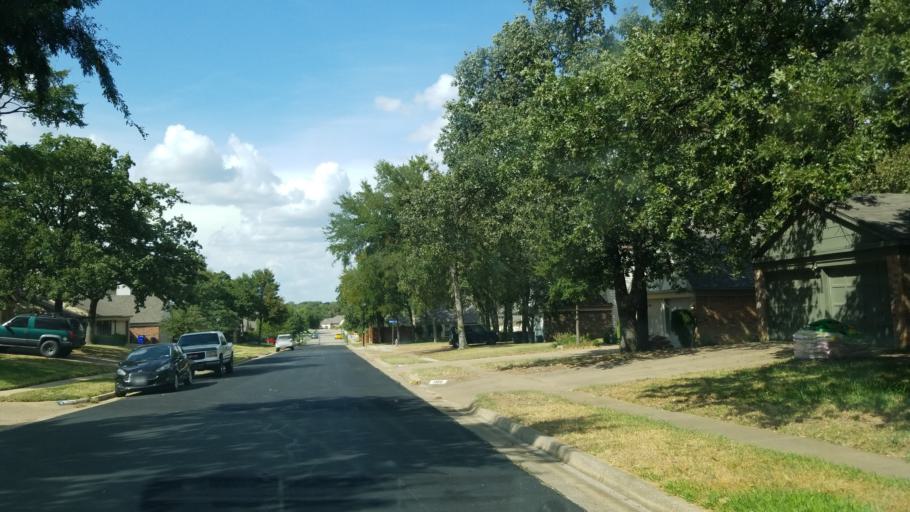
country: US
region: Texas
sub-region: Tarrant County
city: Euless
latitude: 32.8616
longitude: -97.0777
